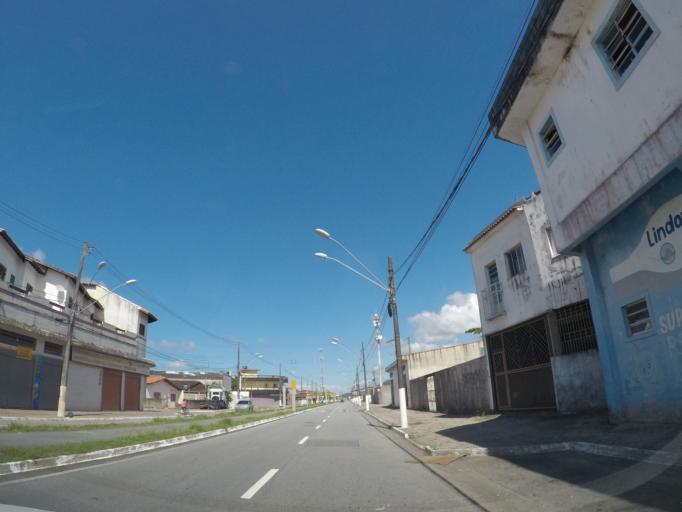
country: BR
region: Sao Paulo
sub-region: Mongagua
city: Mongagua
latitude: -24.0528
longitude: -46.5425
